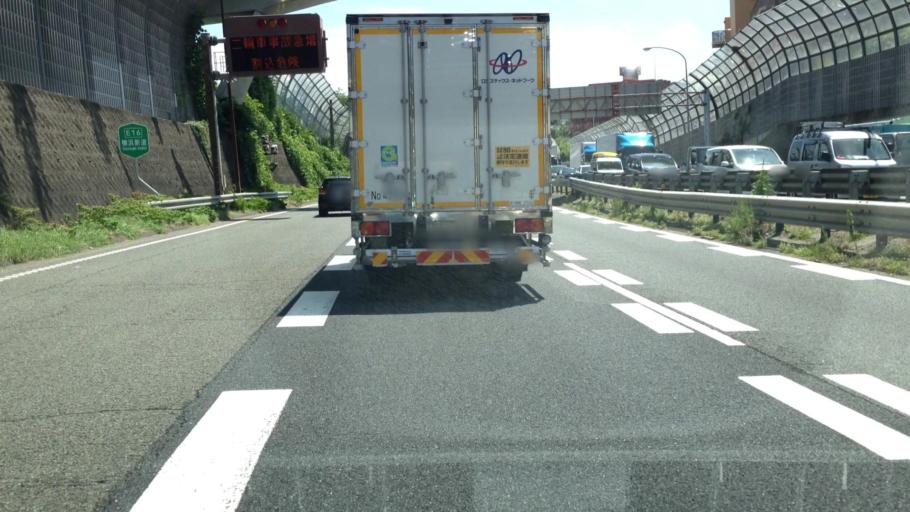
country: JP
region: Kanagawa
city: Yokohama
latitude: 35.4475
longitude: 139.5742
